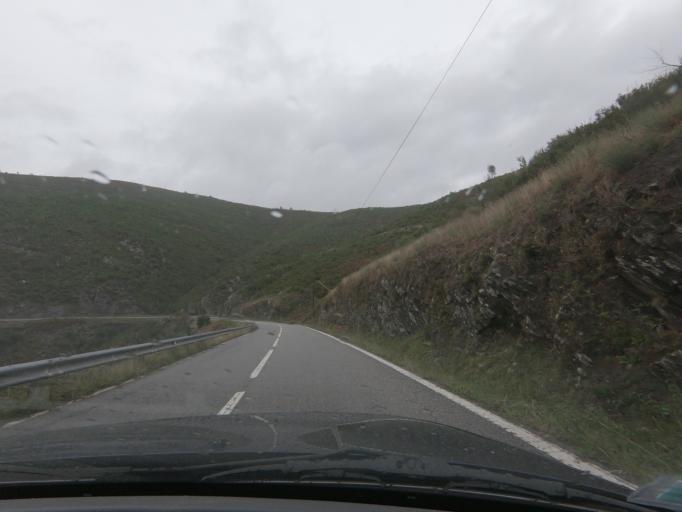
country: PT
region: Vila Real
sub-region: Mondim de Basto
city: Mondim de Basto
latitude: 41.3576
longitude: -7.9158
